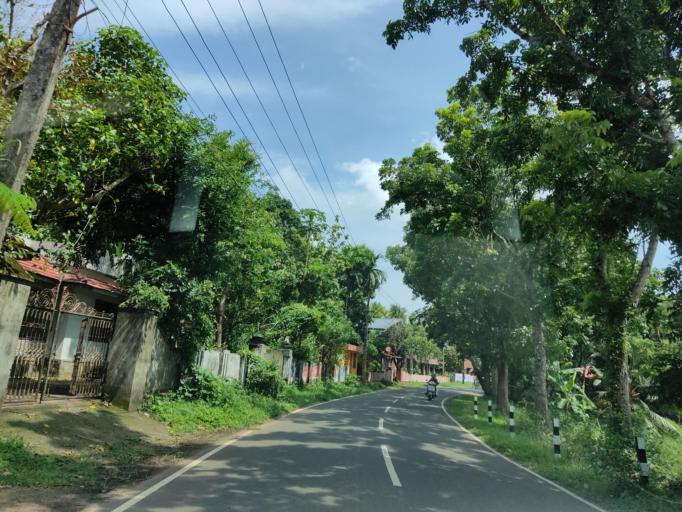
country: IN
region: Kerala
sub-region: Alappuzha
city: Mavelikara
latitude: 9.2881
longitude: 76.5711
